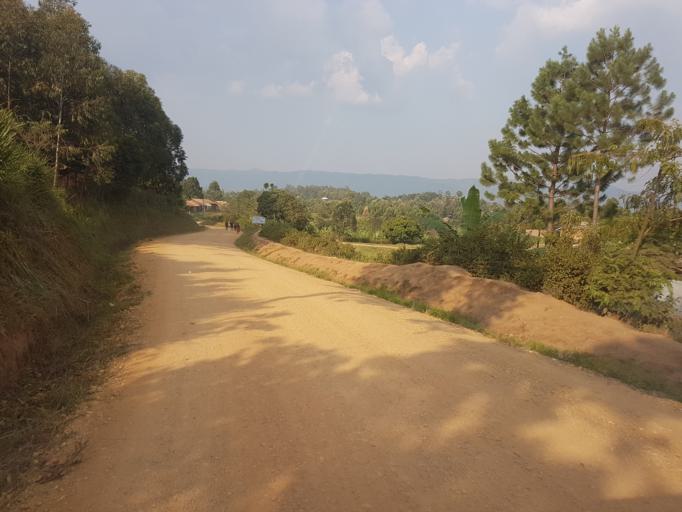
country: UG
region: Western Region
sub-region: Rukungiri District
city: Rukungiri
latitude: -0.6490
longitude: 29.8464
